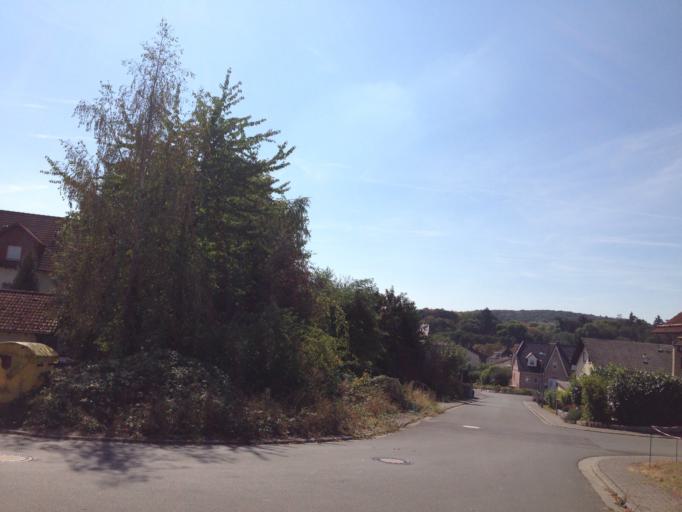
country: DE
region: Hesse
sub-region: Regierungsbezirk Giessen
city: Heuchelheim
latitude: 50.6154
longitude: 8.6105
